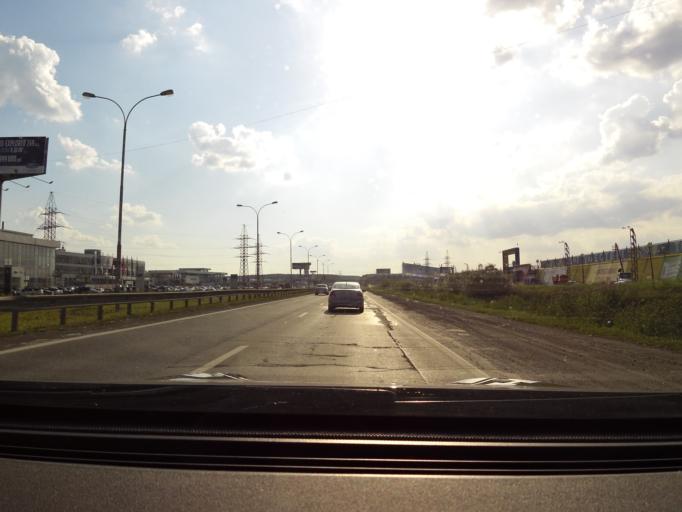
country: RU
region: Sverdlovsk
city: Shirokaya Rechka
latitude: 56.8272
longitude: 60.5212
